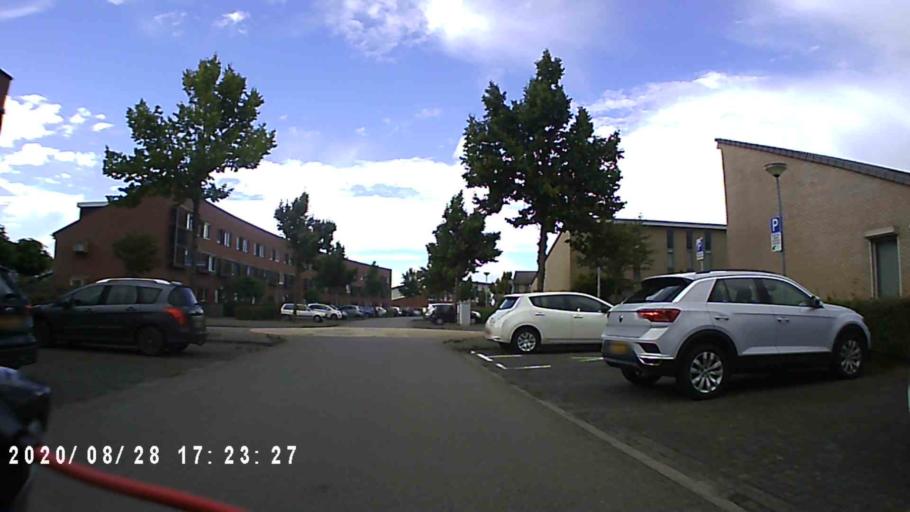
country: NL
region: Groningen
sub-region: Gemeente Groningen
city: Groningen
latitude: 53.2037
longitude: 6.5120
